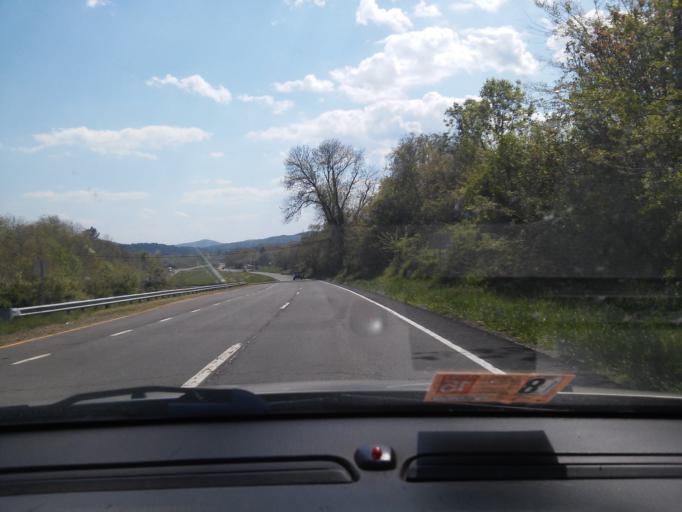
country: US
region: Virginia
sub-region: Rappahannock County
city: Washington
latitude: 38.6717
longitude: -78.2141
